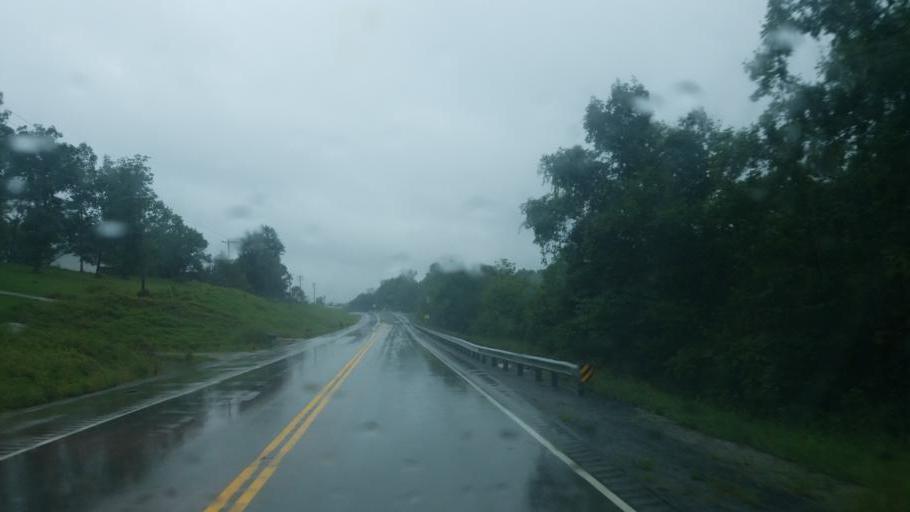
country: US
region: Kentucky
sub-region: Fleming County
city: Flemingsburg
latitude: 38.3382
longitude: -83.5967
